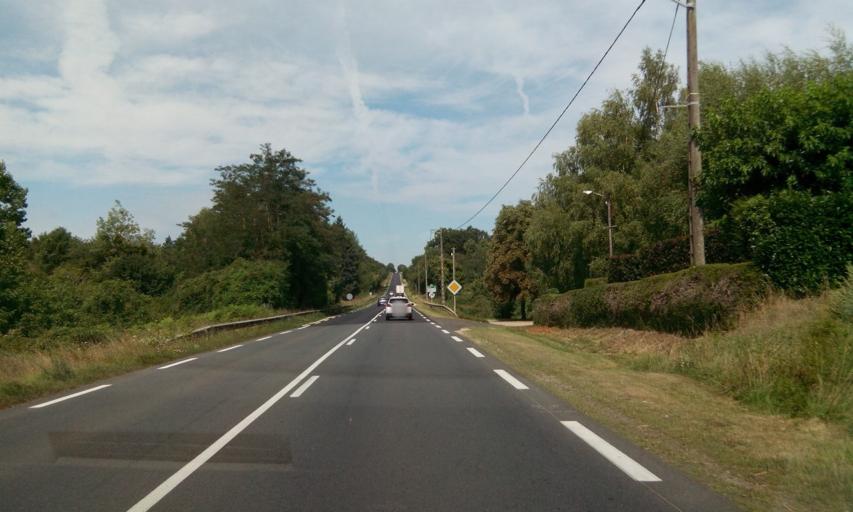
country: FR
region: Poitou-Charentes
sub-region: Departement des Deux-Sevres
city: Sauze-Vaussais
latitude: 46.1389
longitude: 0.0972
